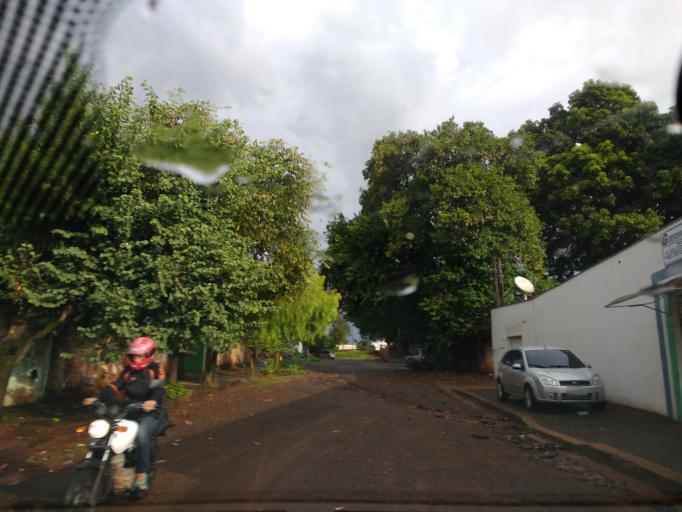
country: BR
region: Parana
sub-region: Londrina
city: Londrina
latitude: -23.2916
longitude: -51.1462
